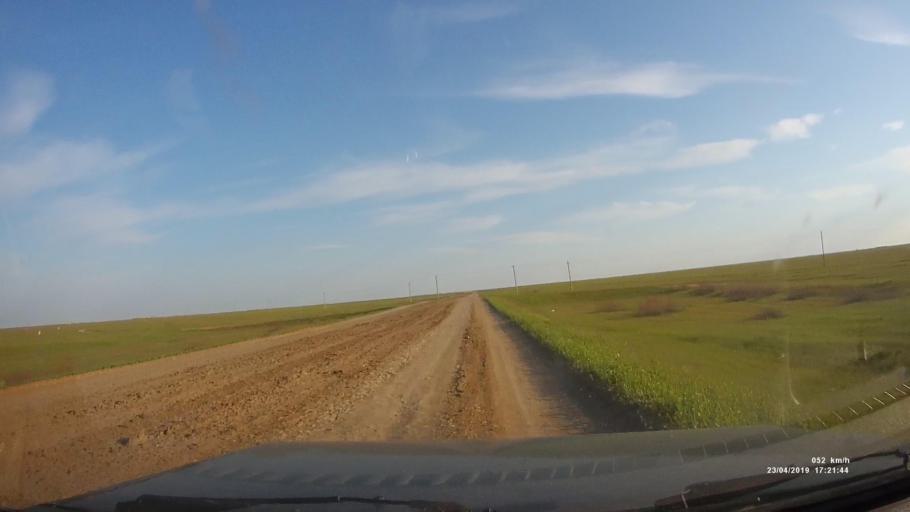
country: RU
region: Kalmykiya
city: Priyutnoye
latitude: 46.1737
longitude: 43.5057
